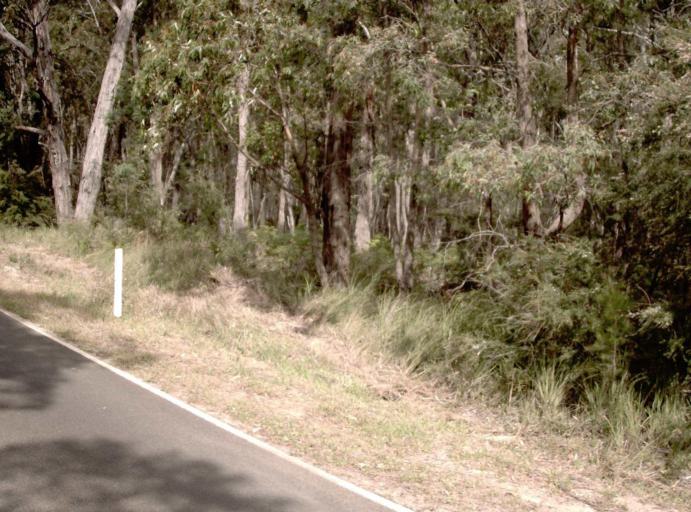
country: AU
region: Victoria
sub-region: Latrobe
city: Traralgon
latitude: -38.3808
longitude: 146.7685
